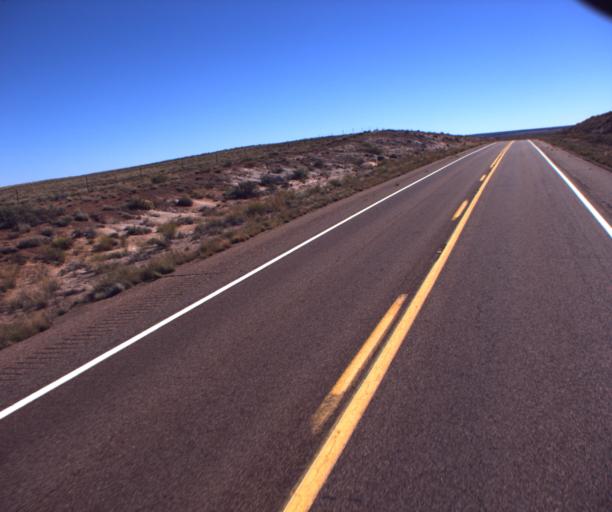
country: US
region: Arizona
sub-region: Navajo County
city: Holbrook
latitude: 34.7781
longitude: -109.8385
